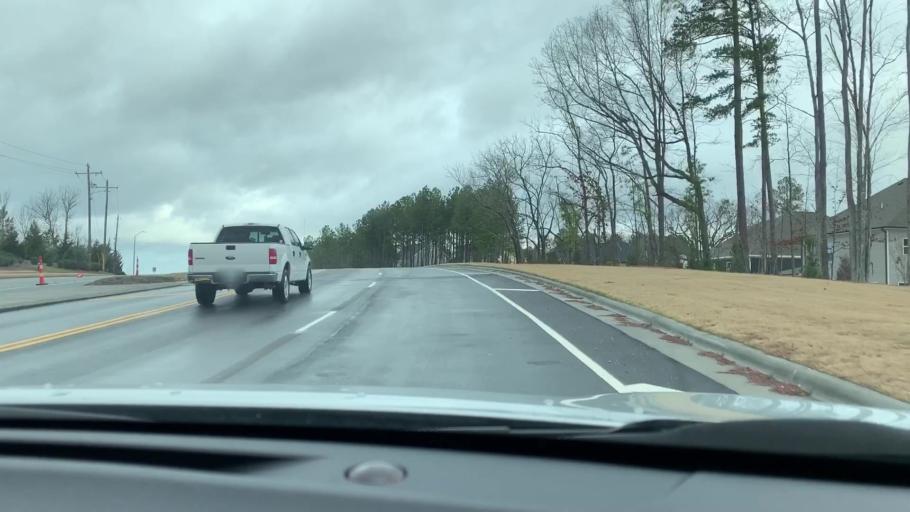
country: US
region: North Carolina
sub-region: Wake County
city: Green Level
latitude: 35.8310
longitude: -78.8992
